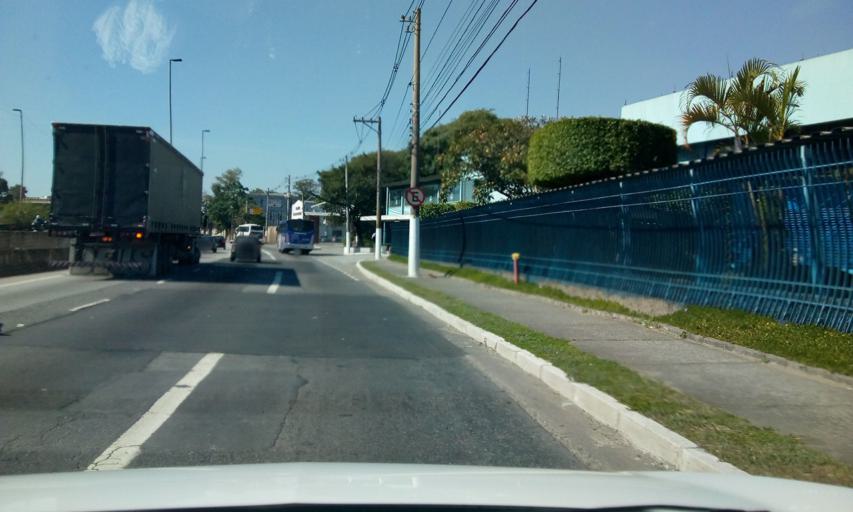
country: BR
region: Sao Paulo
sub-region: Sao Paulo
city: Sao Paulo
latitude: -23.5307
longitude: -46.5913
